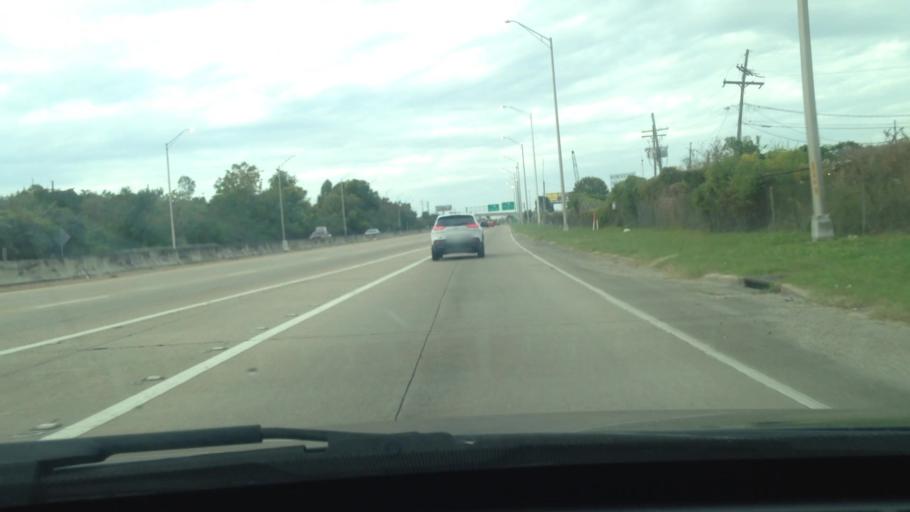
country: US
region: Louisiana
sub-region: Jefferson Parish
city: Jefferson
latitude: 29.9696
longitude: -90.1364
